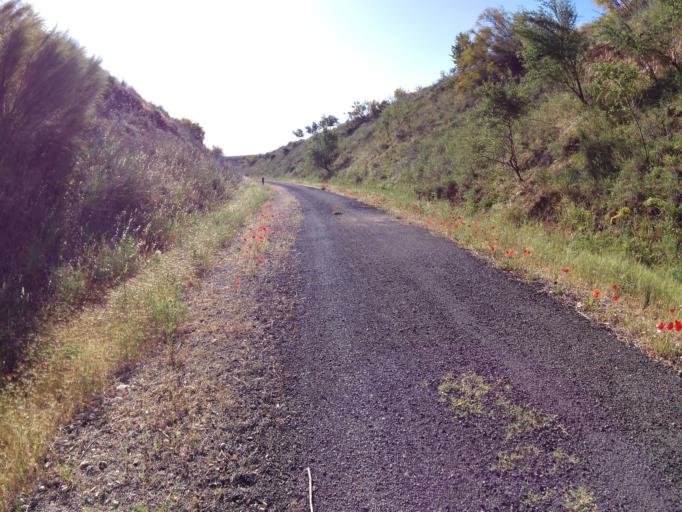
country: ES
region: Andalusia
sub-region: Province of Cordoba
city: Luque
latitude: 37.5647
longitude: -4.2440
